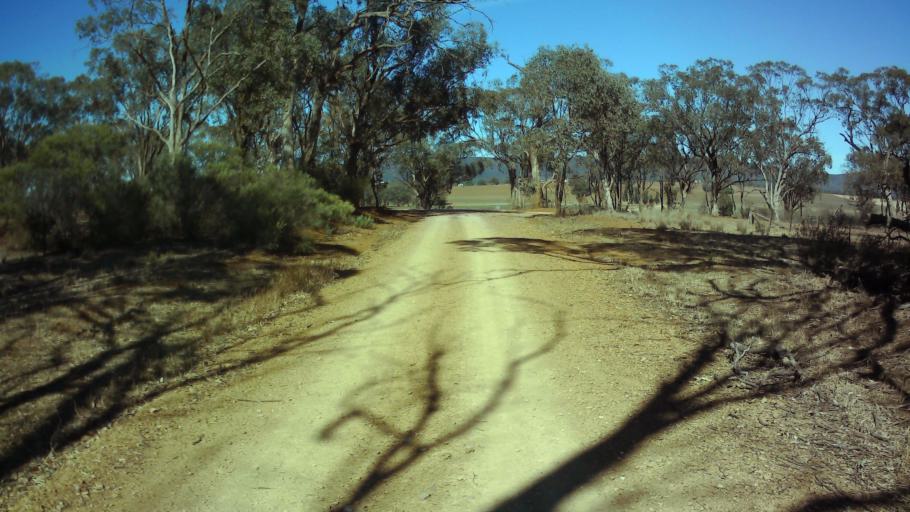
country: AU
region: New South Wales
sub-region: Weddin
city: Grenfell
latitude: -33.9318
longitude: 148.0781
